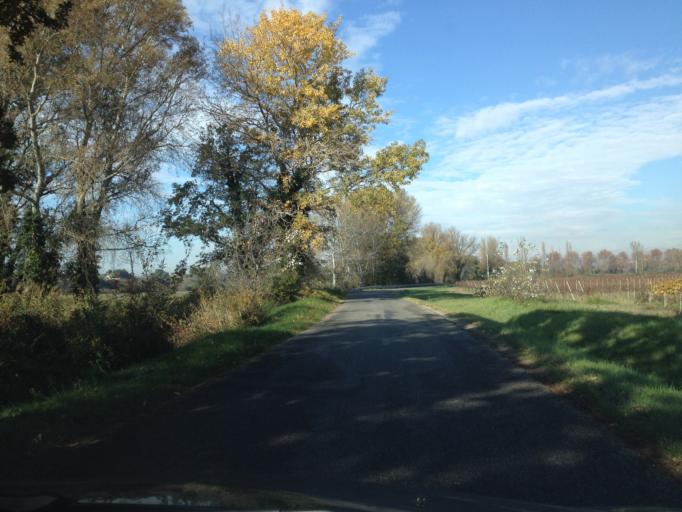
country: FR
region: Provence-Alpes-Cote d'Azur
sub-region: Departement du Vaucluse
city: Bedarrides
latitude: 44.0553
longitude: 4.8976
